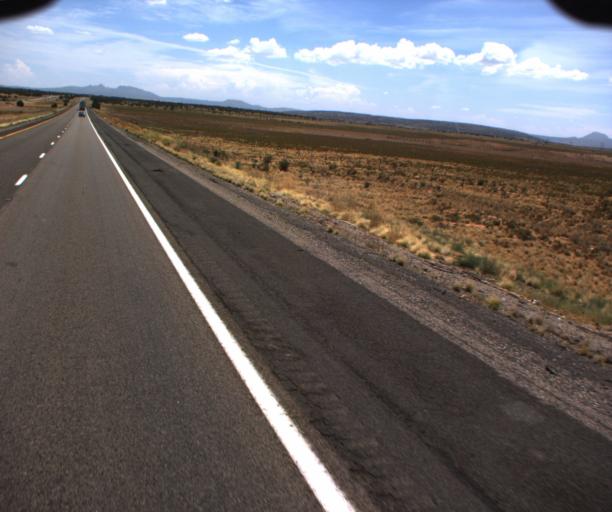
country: US
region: Arizona
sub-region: Mohave County
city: Peach Springs
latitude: 35.3101
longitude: -112.9790
